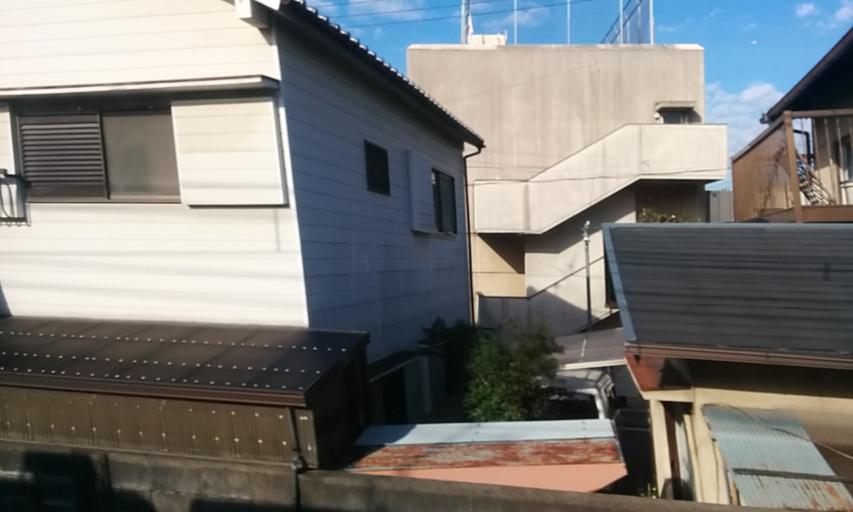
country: JP
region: Kyoto
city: Uji
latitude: 34.8638
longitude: 135.7745
